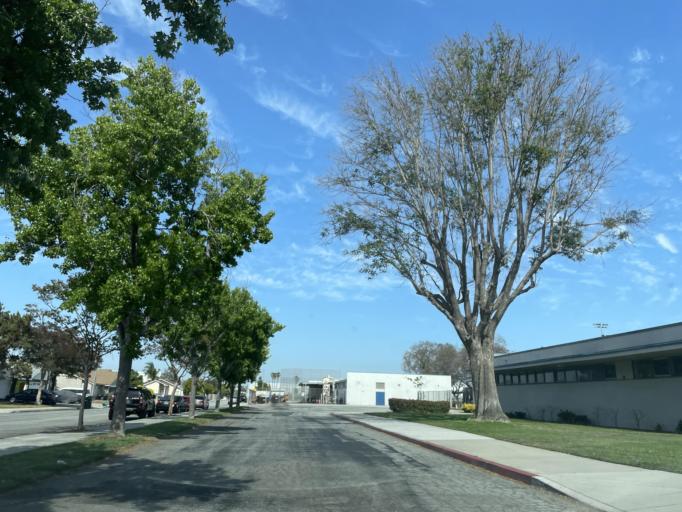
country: US
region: California
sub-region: Los Angeles County
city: Norwalk
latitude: 33.9095
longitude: -118.0546
